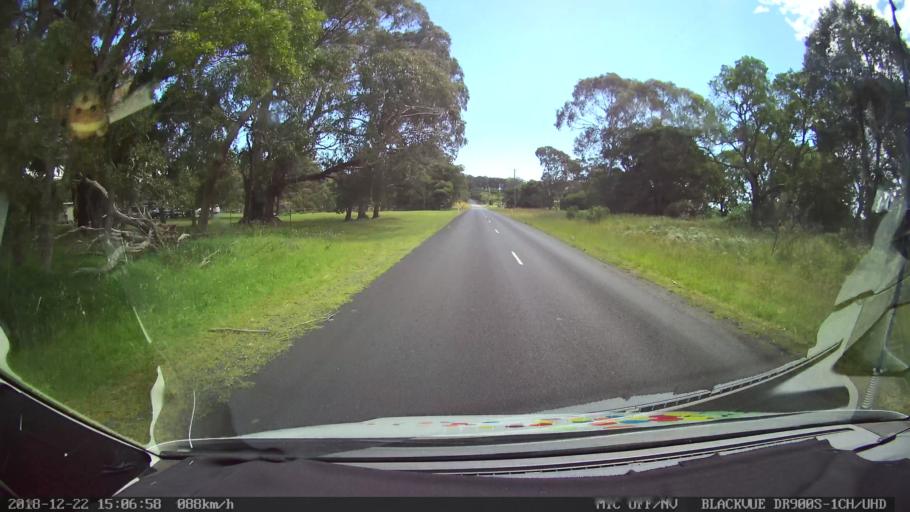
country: AU
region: New South Wales
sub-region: Bellingen
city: Dorrigo
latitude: -30.2969
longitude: 152.4207
